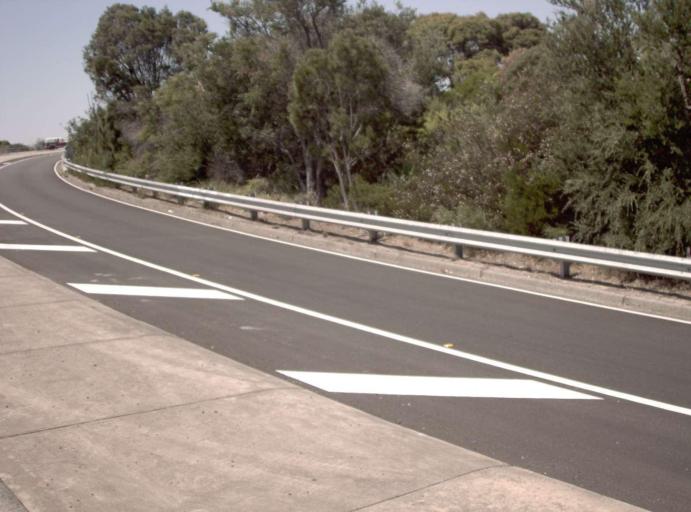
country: AU
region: Victoria
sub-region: Frankston
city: Frankston North
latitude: -38.1196
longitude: 145.1356
